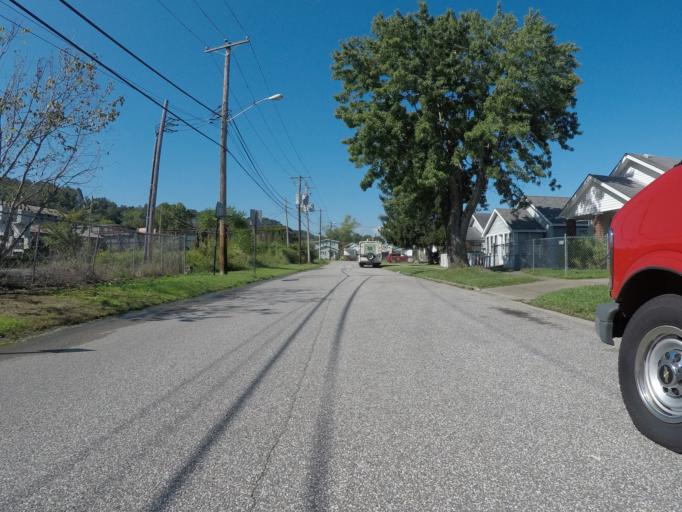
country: US
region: Ohio
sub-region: Lawrence County
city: Burlington
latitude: 38.4005
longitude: -82.4988
